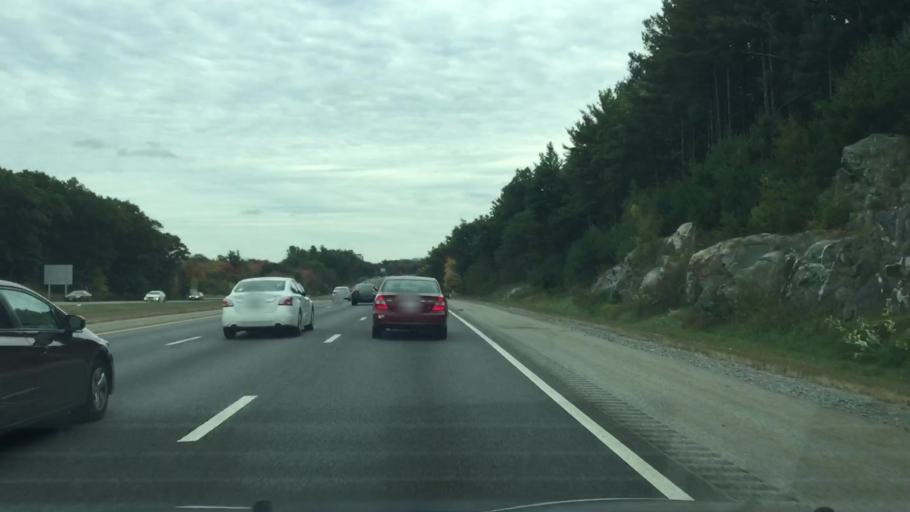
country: US
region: Massachusetts
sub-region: Middlesex County
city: Pinehurst
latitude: 42.4932
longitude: -71.2346
